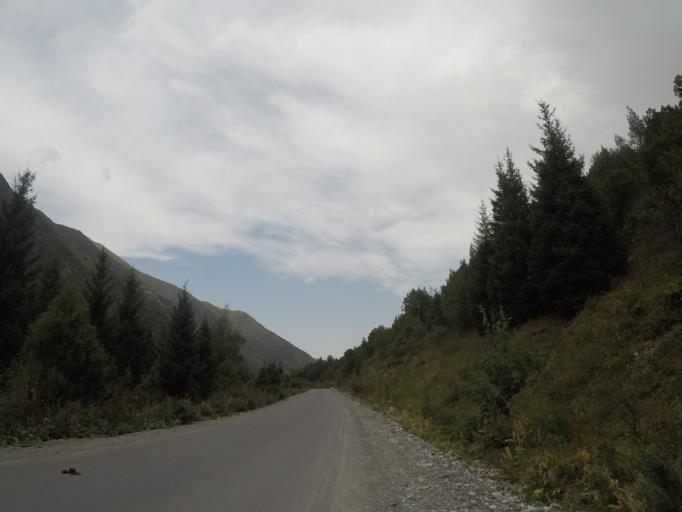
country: KG
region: Chuy
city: Bishkek
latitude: 42.5866
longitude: 74.4841
